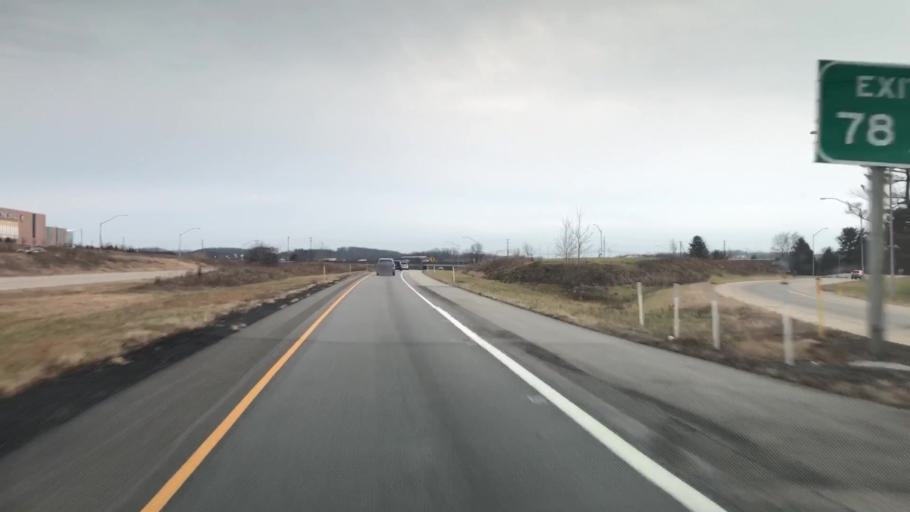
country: US
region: Pennsylvania
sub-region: Butler County
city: Cranberry Township
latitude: 40.6899
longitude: -80.0972
